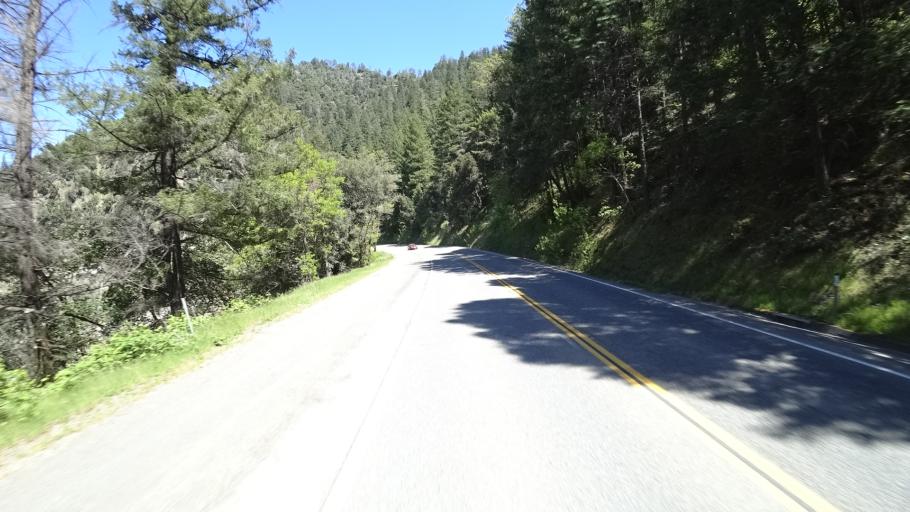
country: US
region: California
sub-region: Trinity County
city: Hayfork
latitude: 40.7759
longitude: -123.3090
